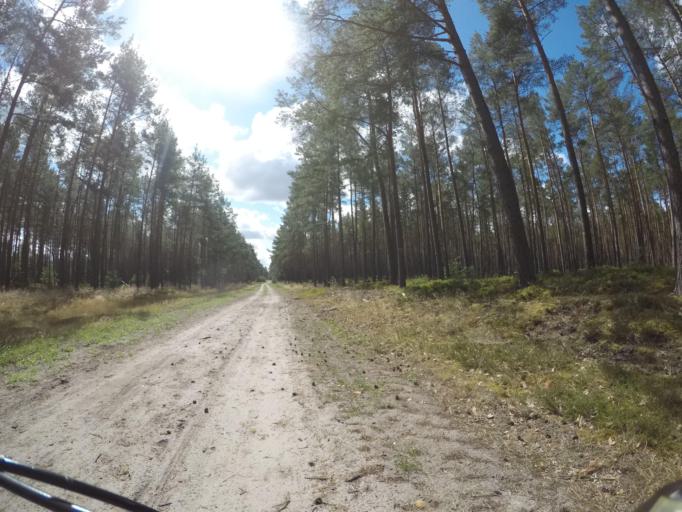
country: DE
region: Lower Saxony
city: Hitzacker
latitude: 53.2252
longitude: 11.0334
